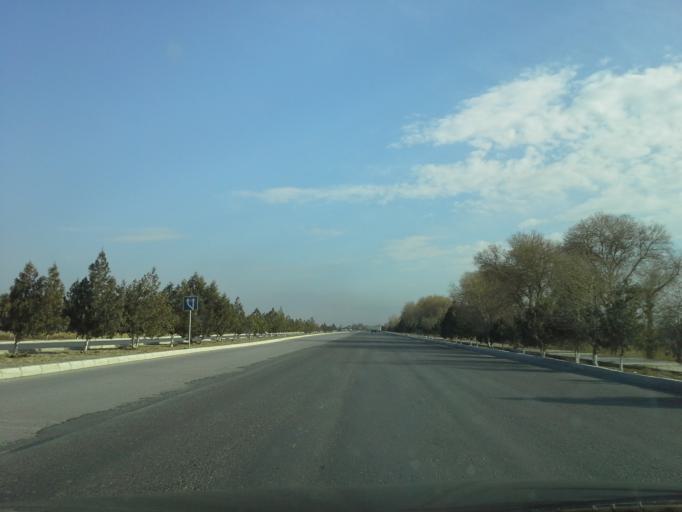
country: TM
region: Ahal
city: Abadan
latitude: 38.0775
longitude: 58.2301
